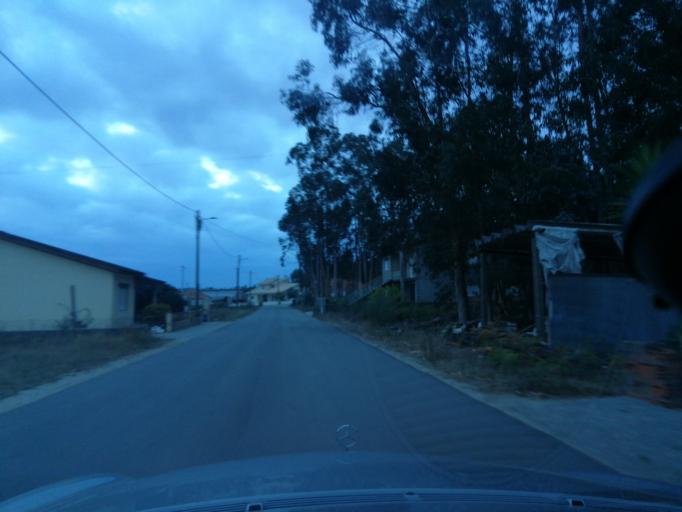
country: PT
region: Aveiro
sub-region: Estarreja
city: Estarreja
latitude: 40.7665
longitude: -8.5932
